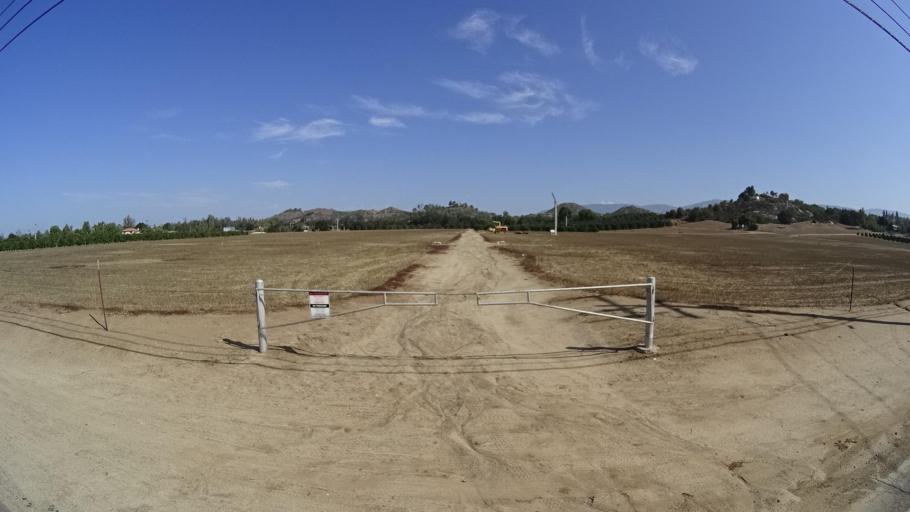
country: US
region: California
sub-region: San Diego County
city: Valley Center
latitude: 33.2356
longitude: -117.0003
